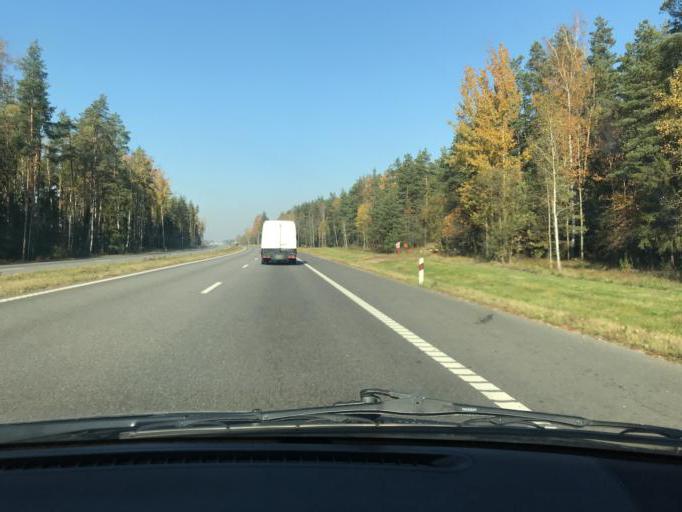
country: BY
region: Minsk
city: Slutsk
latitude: 53.3350
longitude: 27.5285
